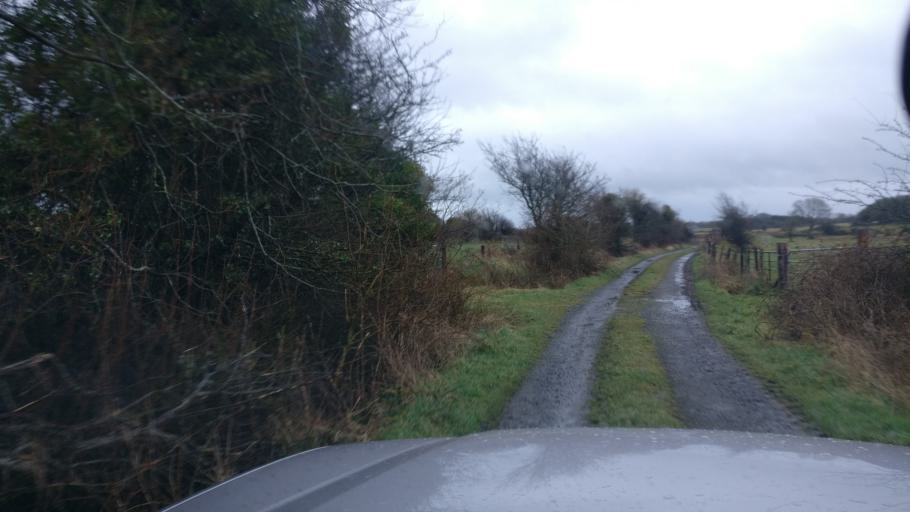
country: IE
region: Connaught
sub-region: County Galway
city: Ballinasloe
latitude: 53.2503
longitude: -8.3241
